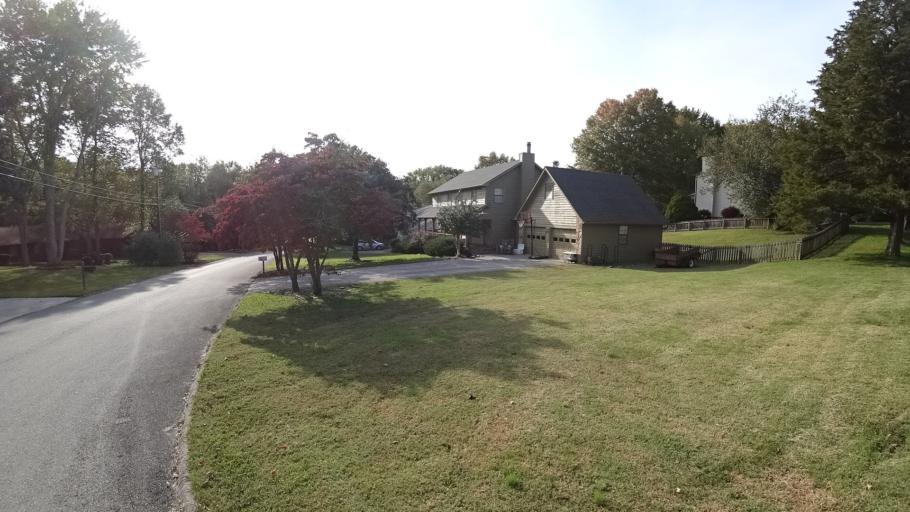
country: US
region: Tennessee
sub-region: Knox County
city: Farragut
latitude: 35.9077
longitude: -84.1611
